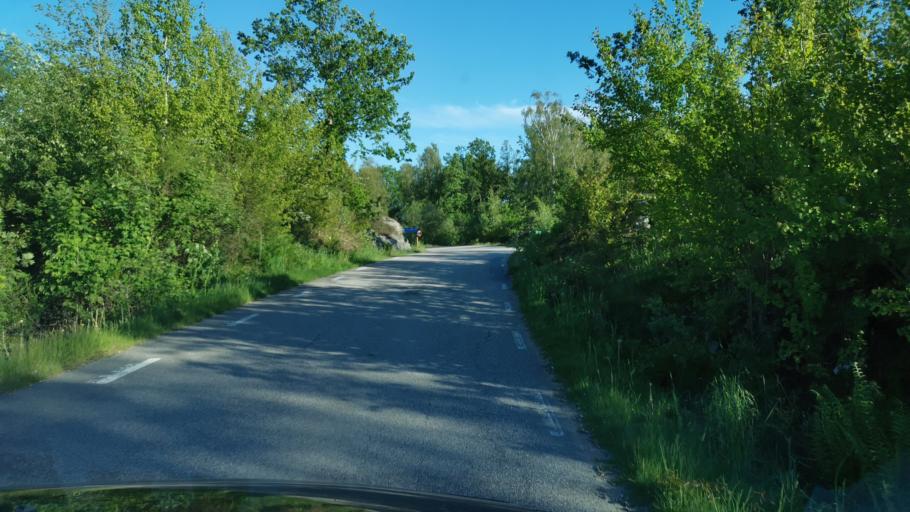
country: SE
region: Vaestra Goetaland
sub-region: Orust
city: Henan
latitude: 58.2657
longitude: 11.6078
